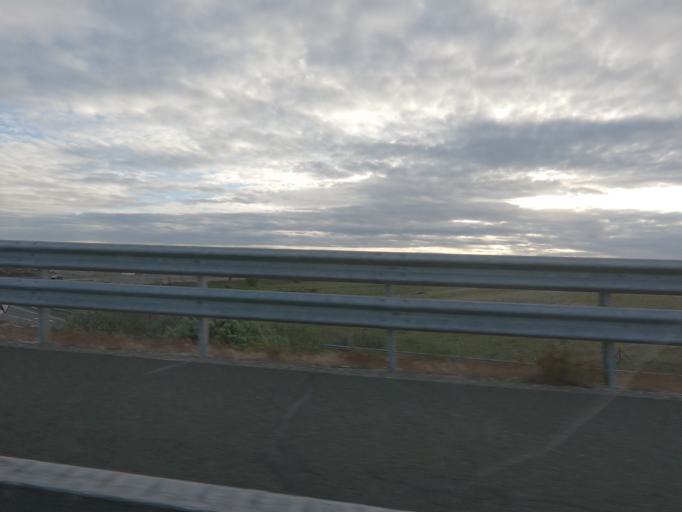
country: ES
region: Extremadura
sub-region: Provincia de Caceres
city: Caceres
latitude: 39.4633
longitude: -6.4223
